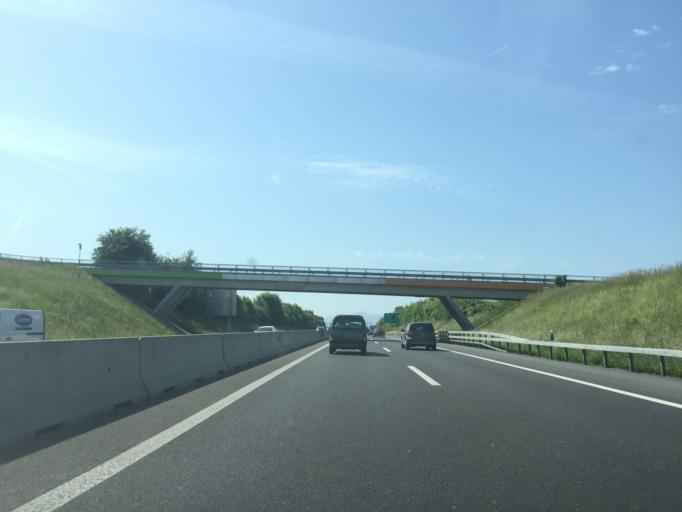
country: CH
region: Vaud
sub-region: Gros-de-Vaud District
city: Penthalaz
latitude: 46.5896
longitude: 6.5542
